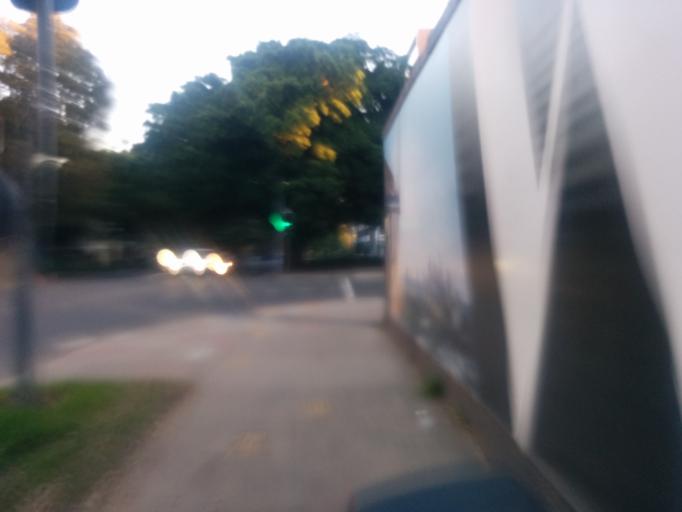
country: AU
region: New South Wales
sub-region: City of Sydney
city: Alexandria
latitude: -33.9034
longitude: 151.2097
